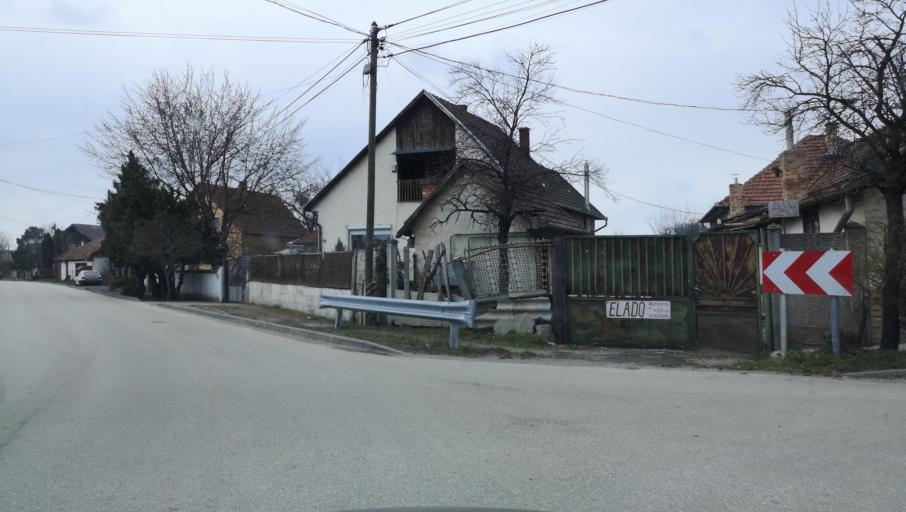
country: HU
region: Pest
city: Monor
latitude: 47.3582
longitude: 19.4434
